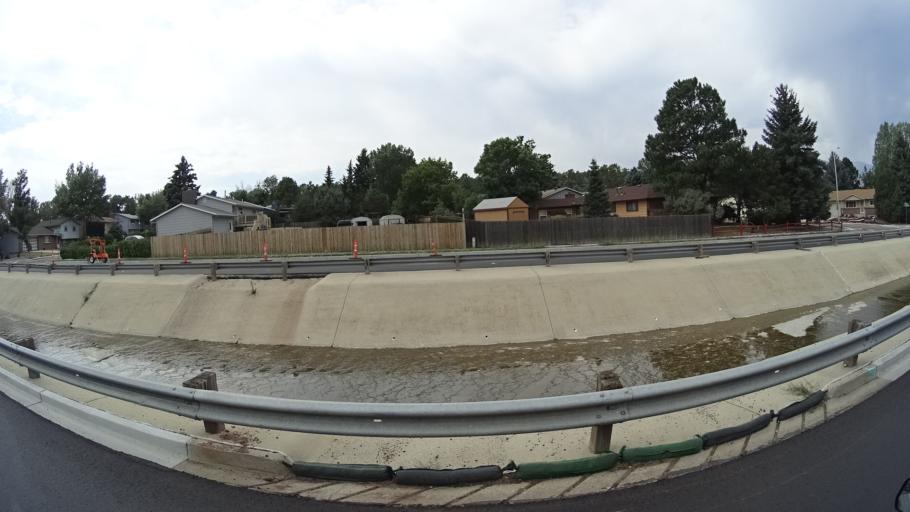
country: US
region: Colorado
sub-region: El Paso County
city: Colorado Springs
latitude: 38.9249
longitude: -104.7987
